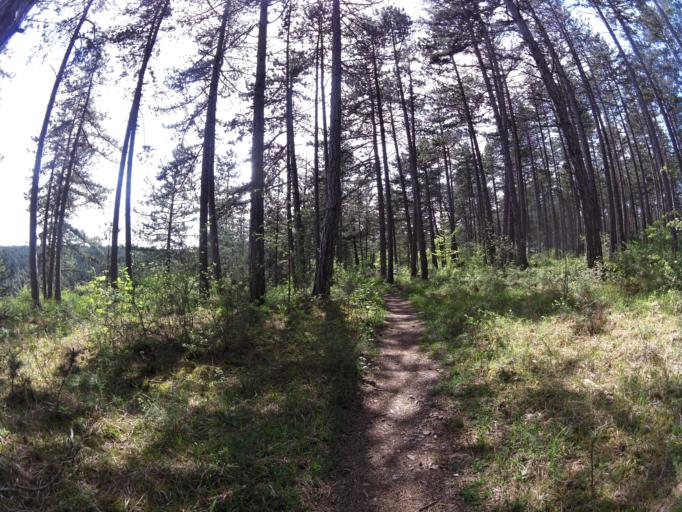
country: DE
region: Bavaria
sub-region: Regierungsbezirk Unterfranken
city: Erlabrunn
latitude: 49.8597
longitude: 9.8316
